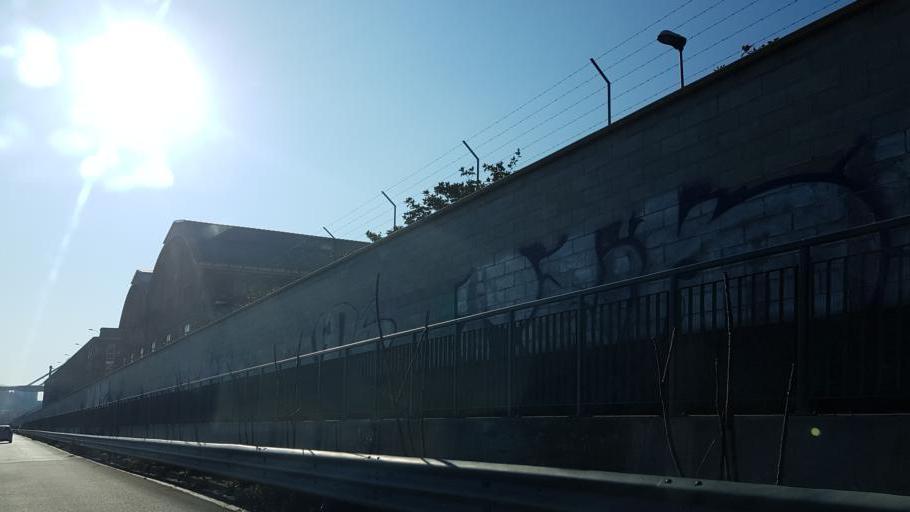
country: IT
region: Liguria
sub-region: Provincia di Genova
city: Genoa
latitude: 44.4340
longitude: 8.8895
